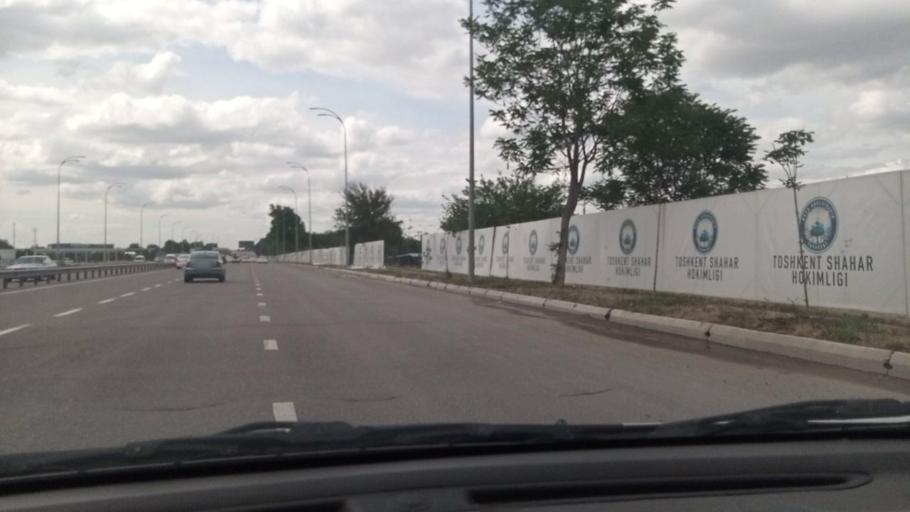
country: UZ
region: Toshkent Shahri
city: Bektemir
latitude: 41.2638
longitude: 69.3721
